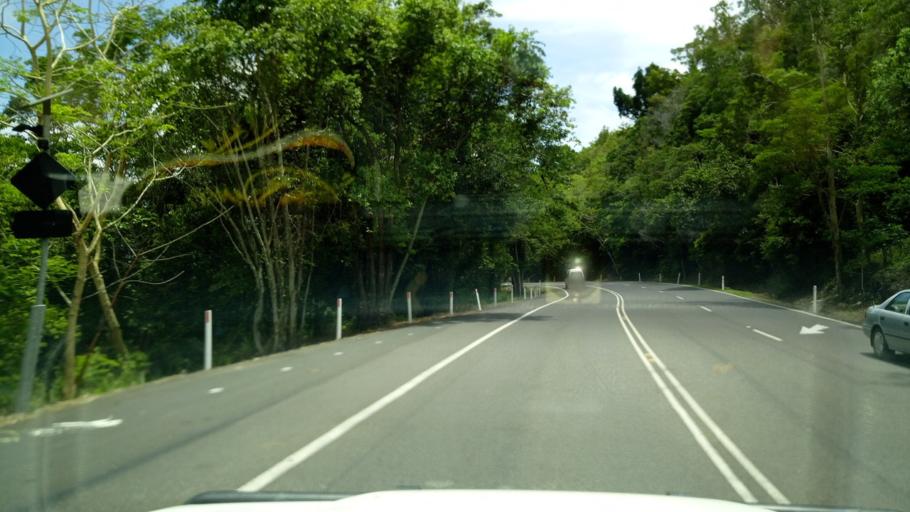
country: AU
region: Queensland
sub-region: Cairns
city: Redlynch
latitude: -16.8495
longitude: 145.6829
